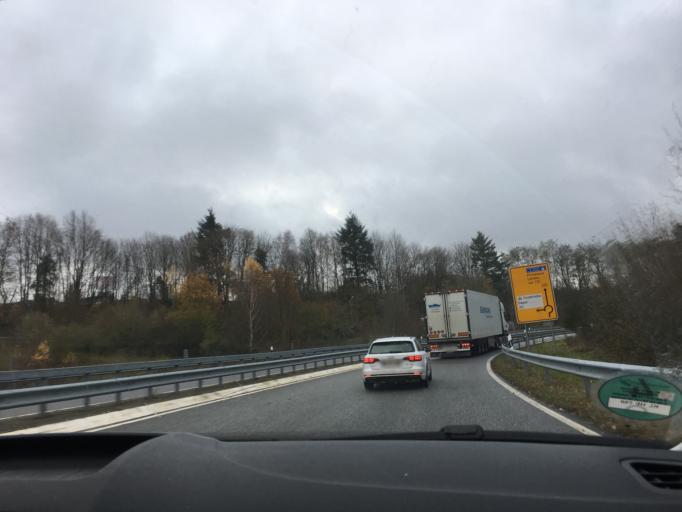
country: DE
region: Rheinland-Pfalz
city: Pirmasens
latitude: 49.2159
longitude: 7.6054
